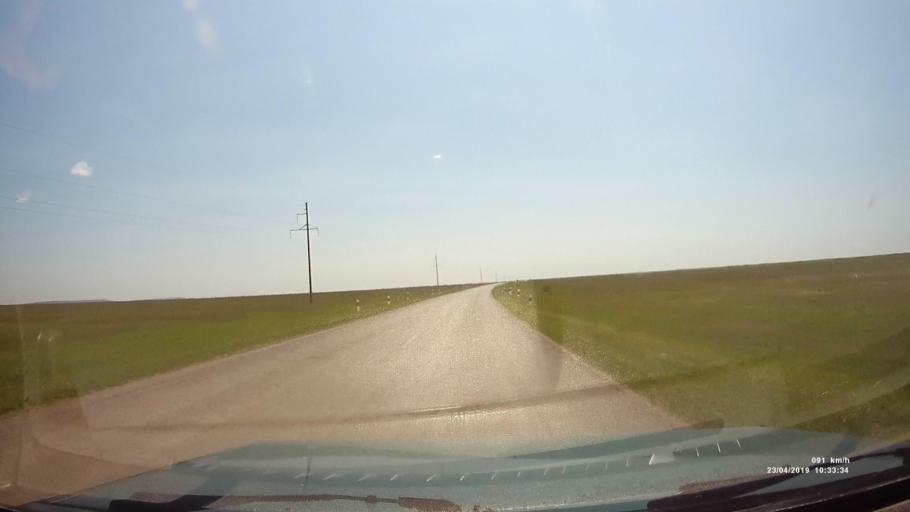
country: RU
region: Kalmykiya
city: Yashalta
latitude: 46.5724
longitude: 42.5986
